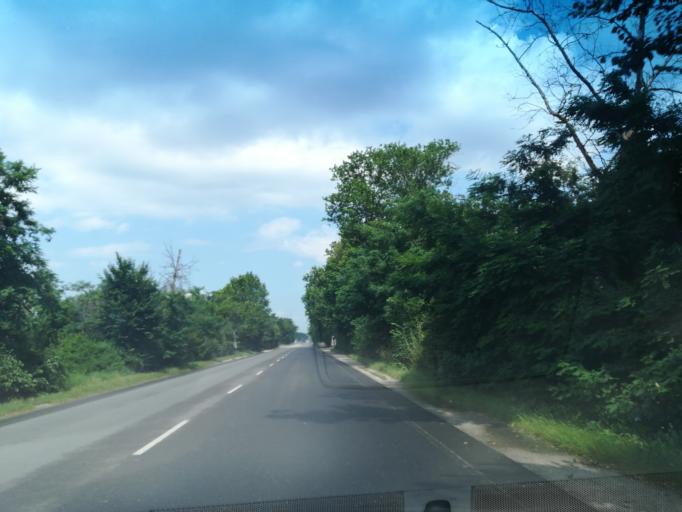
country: BG
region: Plovdiv
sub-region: Obshtina Plovdiv
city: Plovdiv
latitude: 42.1538
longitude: 24.7014
